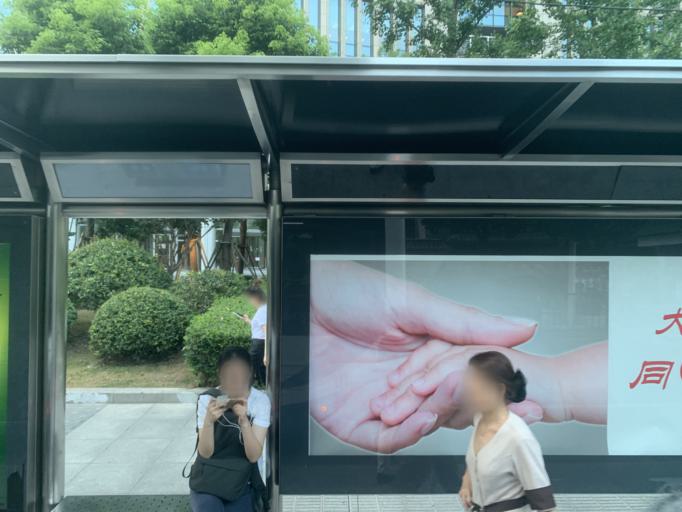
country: CN
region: Shanghai Shi
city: Pudong
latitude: 31.2313
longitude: 121.5245
